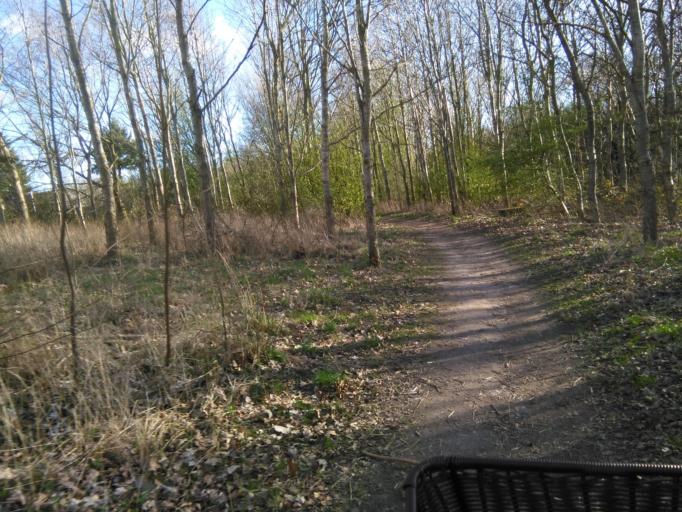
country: DK
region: Central Jutland
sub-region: Arhus Kommune
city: Beder
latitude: 56.0620
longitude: 10.1979
